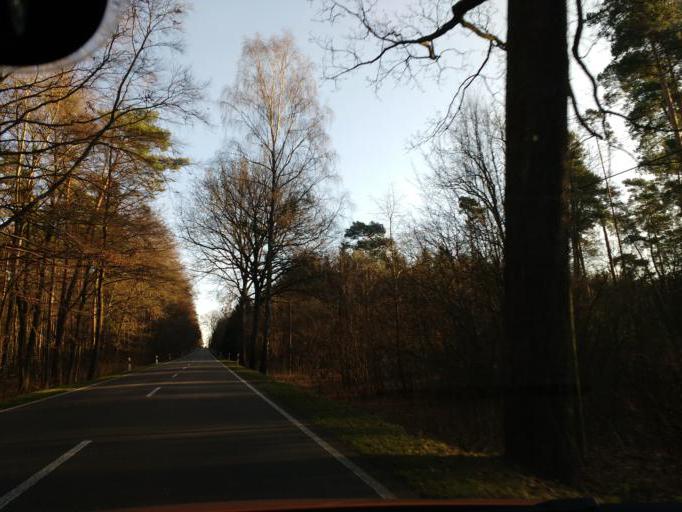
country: DE
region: Brandenburg
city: Protzel
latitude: 52.6449
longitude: 13.9418
